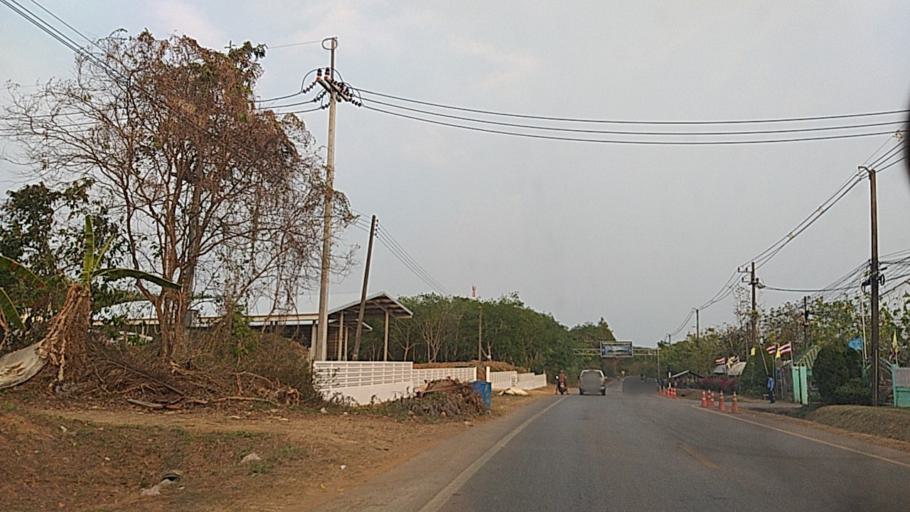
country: TH
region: Trat
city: Laem Ngop
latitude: 12.1911
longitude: 102.2941
